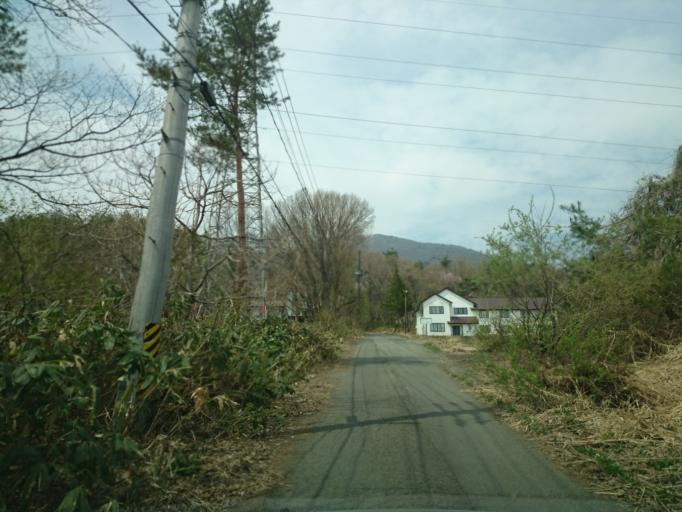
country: JP
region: Fukushima
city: Inawashiro
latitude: 37.5748
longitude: 140.0999
